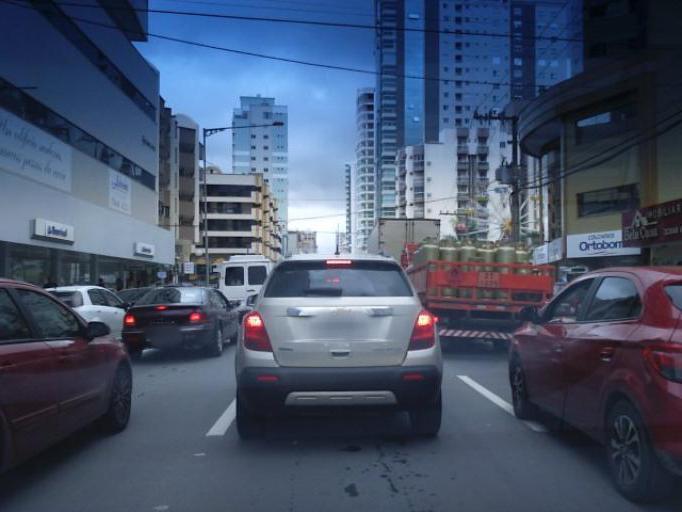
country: BR
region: Santa Catarina
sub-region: Itapema
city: Itapema
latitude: -27.1240
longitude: -48.6046
